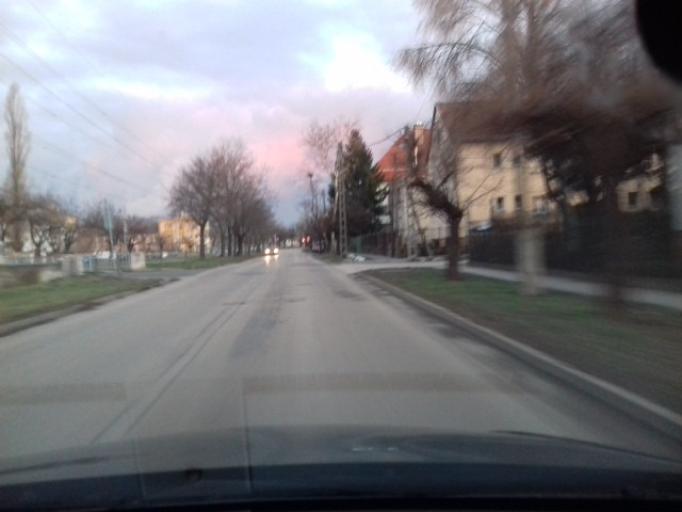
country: HU
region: Budapest
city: Budapest XIV. keruelet
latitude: 47.5263
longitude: 19.1131
